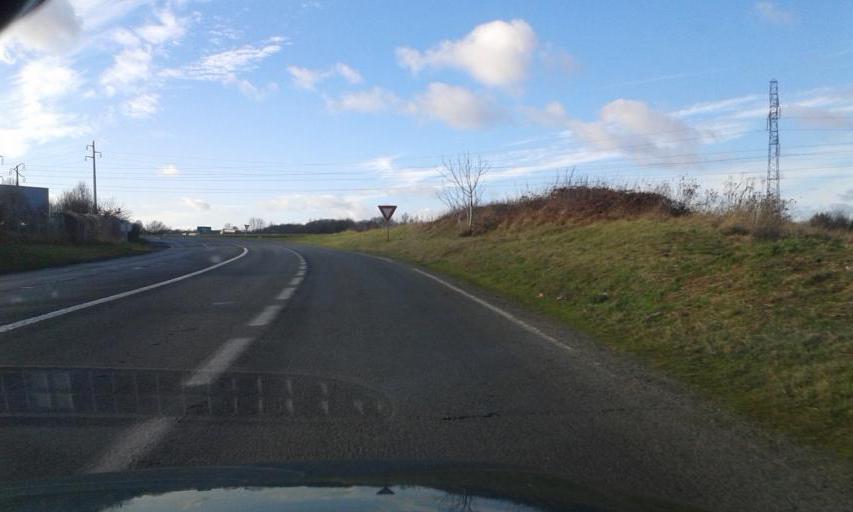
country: FR
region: Picardie
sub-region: Departement de l'Oise
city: Jaux
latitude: 49.4110
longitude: 2.7807
